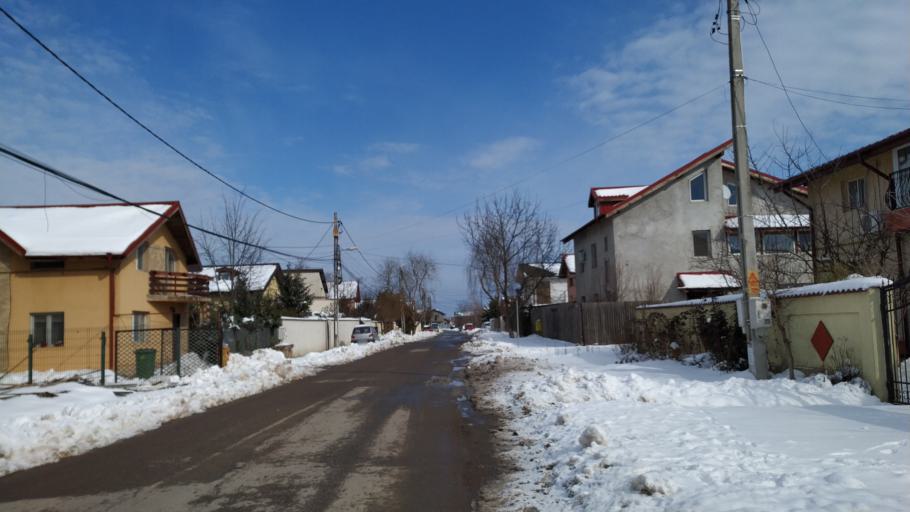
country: RO
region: Ilfov
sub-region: Comuna Berceni
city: Berceni
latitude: 44.3203
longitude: 26.1924
